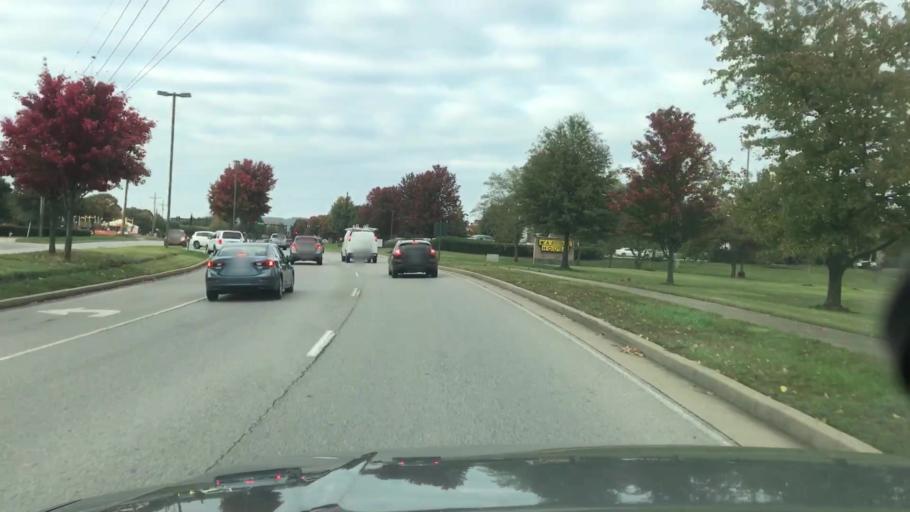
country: US
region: Tennessee
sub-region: Williamson County
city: Franklin
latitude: 35.9451
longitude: -86.8194
